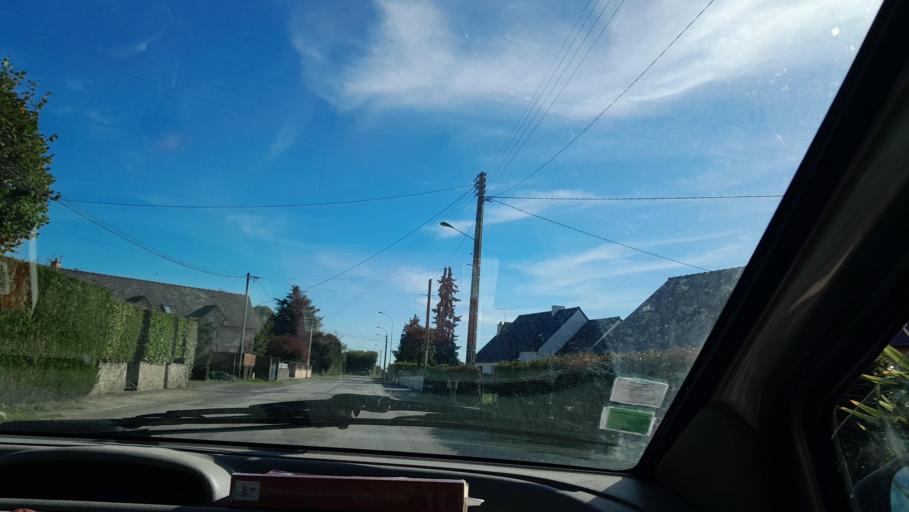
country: FR
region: Brittany
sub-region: Departement d'Ille-et-Vilaine
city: Argentre-du-Plessis
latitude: 48.0497
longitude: -1.1486
